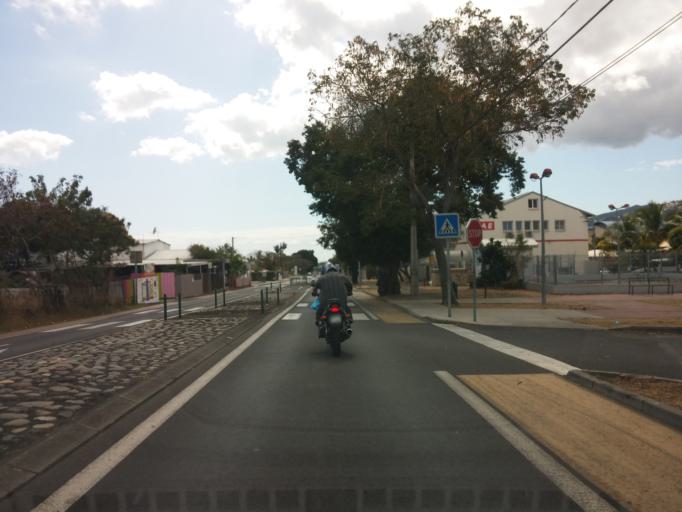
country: RE
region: Reunion
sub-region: Reunion
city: La Possession
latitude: -20.9493
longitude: 55.3263
